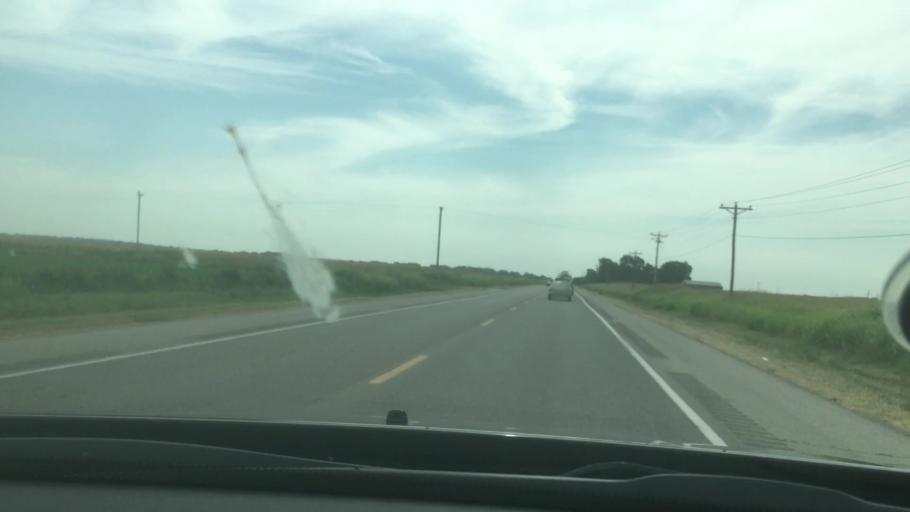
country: US
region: Oklahoma
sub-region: Garvin County
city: Lindsay
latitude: 34.8263
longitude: -97.5515
